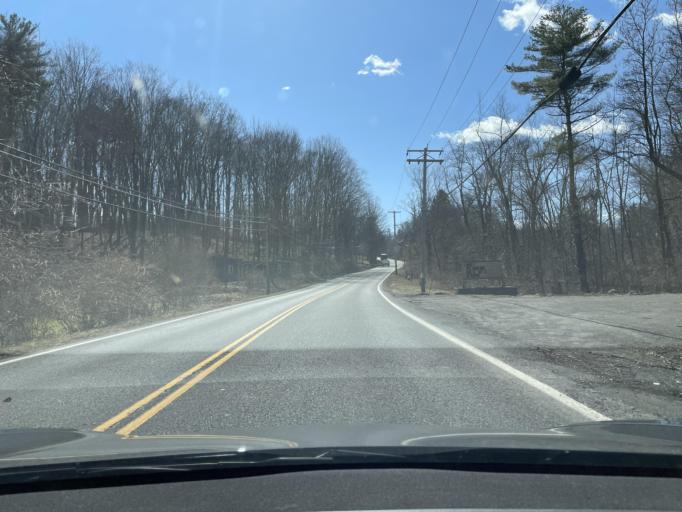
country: US
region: New York
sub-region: Ulster County
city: West Hurley
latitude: 42.0040
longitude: -74.1051
